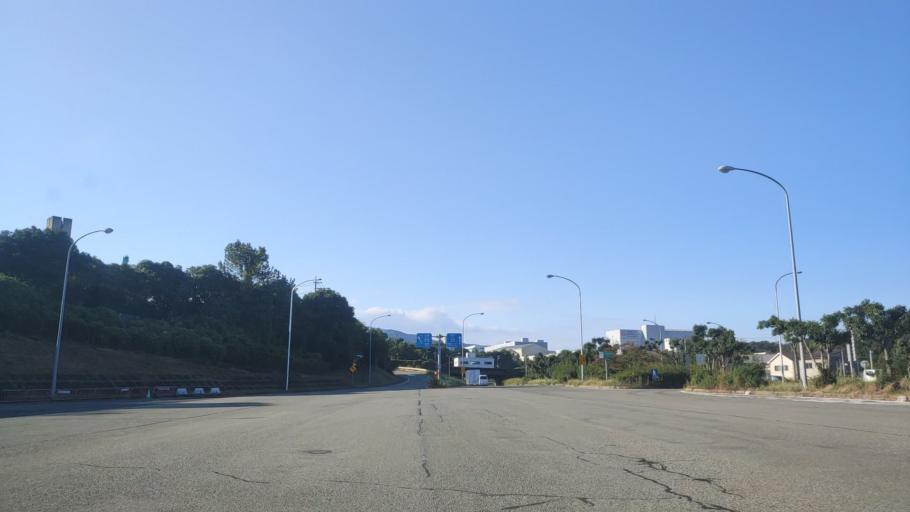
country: JP
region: Hyogo
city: Sandacho
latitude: 34.8360
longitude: 135.2353
